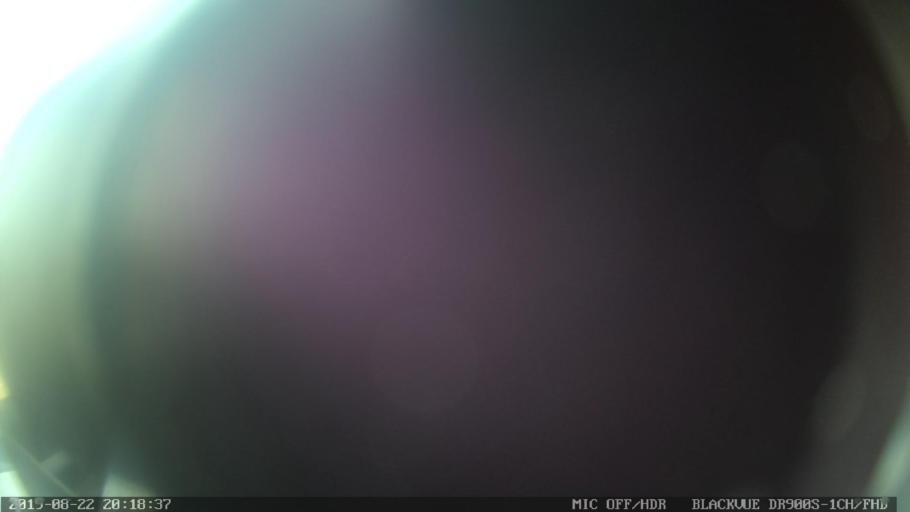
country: PT
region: Guarda
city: Alcains
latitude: 39.9179
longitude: -7.4739
